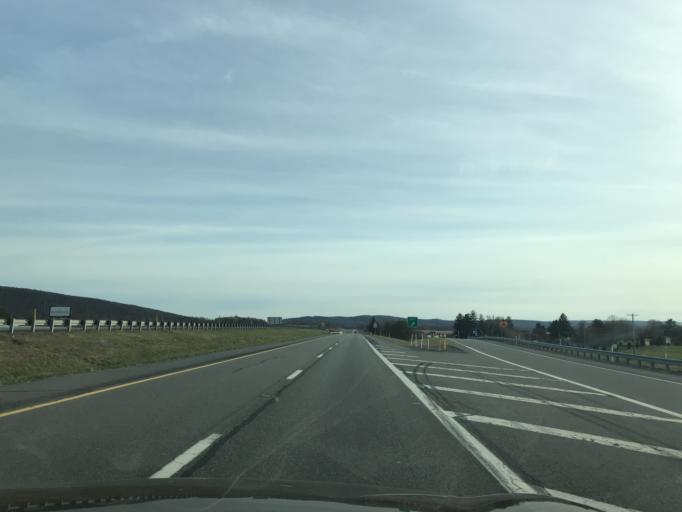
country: US
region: Pennsylvania
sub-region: Union County
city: Lewisburg
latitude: 40.9677
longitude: -76.8422
